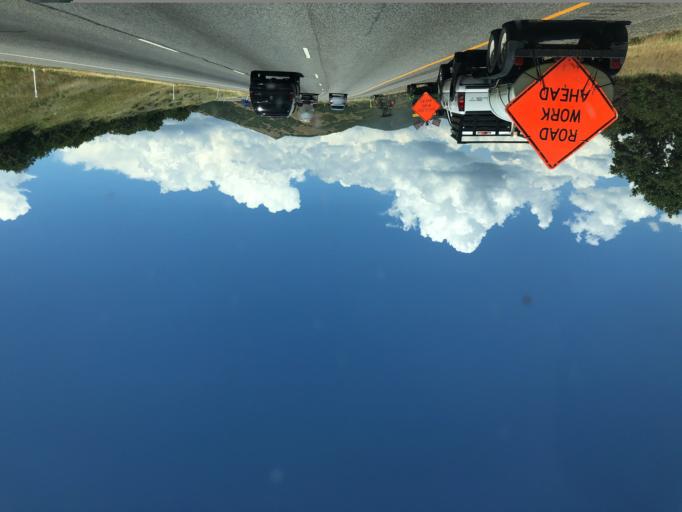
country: US
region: Utah
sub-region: Summit County
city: Summit Park
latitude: 40.7483
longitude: -111.7060
